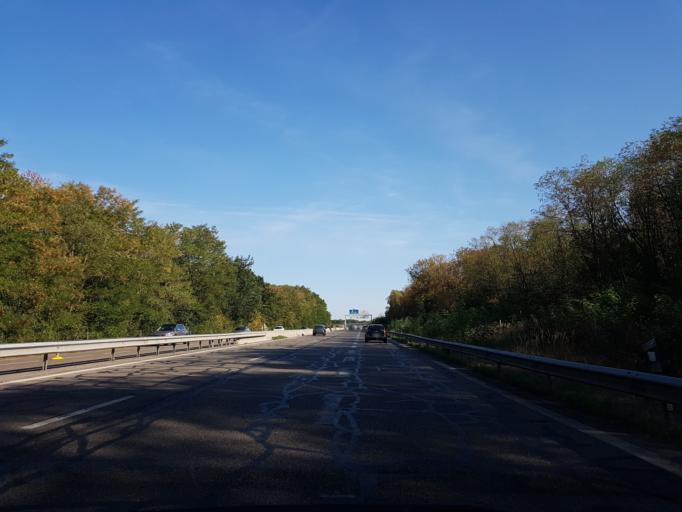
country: FR
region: Alsace
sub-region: Departement du Haut-Rhin
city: Pulversheim
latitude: 47.8247
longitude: 7.2875
